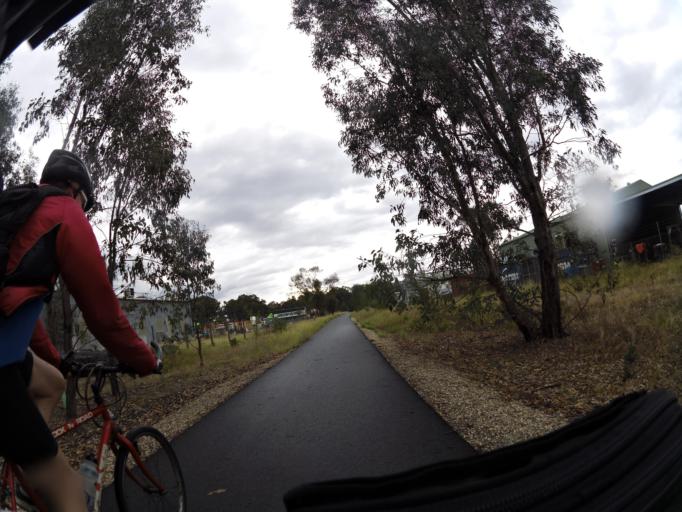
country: AU
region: Victoria
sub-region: Wodonga
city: Wodonga
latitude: -36.1358
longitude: 146.9029
